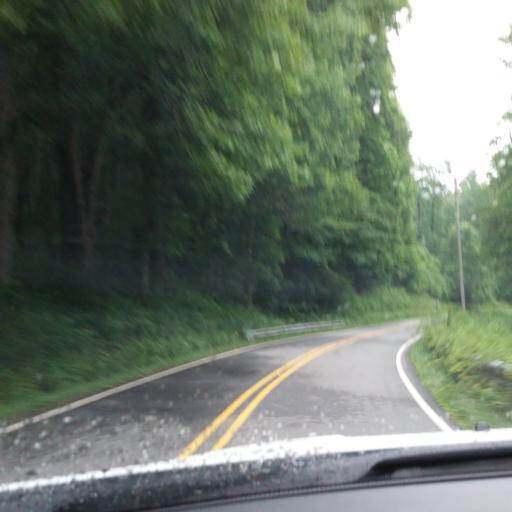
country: US
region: North Carolina
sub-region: Mitchell County
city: Spruce Pine
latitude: 35.7725
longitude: -82.1765
